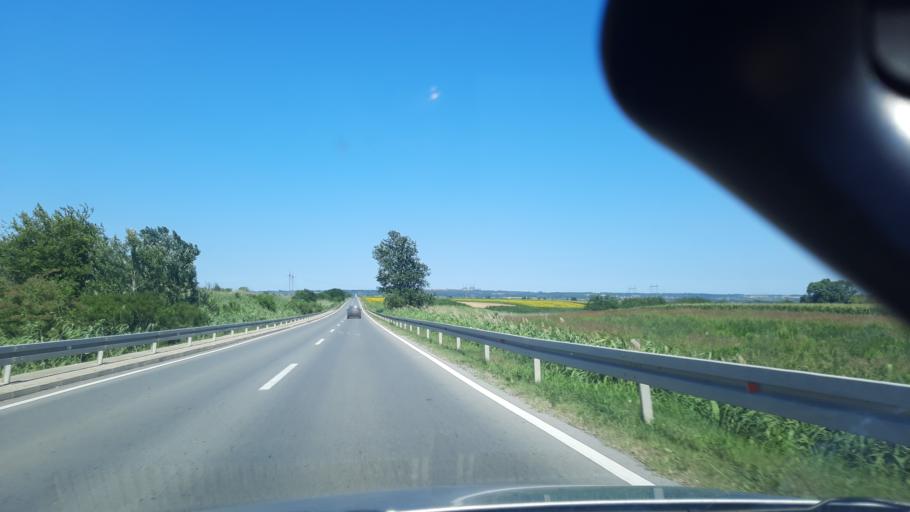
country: RS
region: Central Serbia
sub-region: Branicevski Okrug
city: Pozarevac
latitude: 44.6517
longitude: 21.2676
